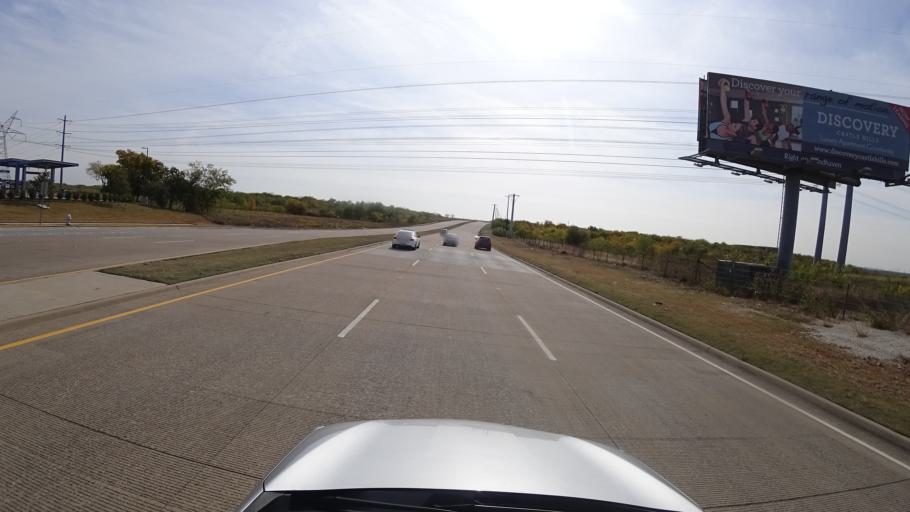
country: US
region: Texas
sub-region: Denton County
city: The Colony
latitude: 33.0607
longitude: -96.8862
